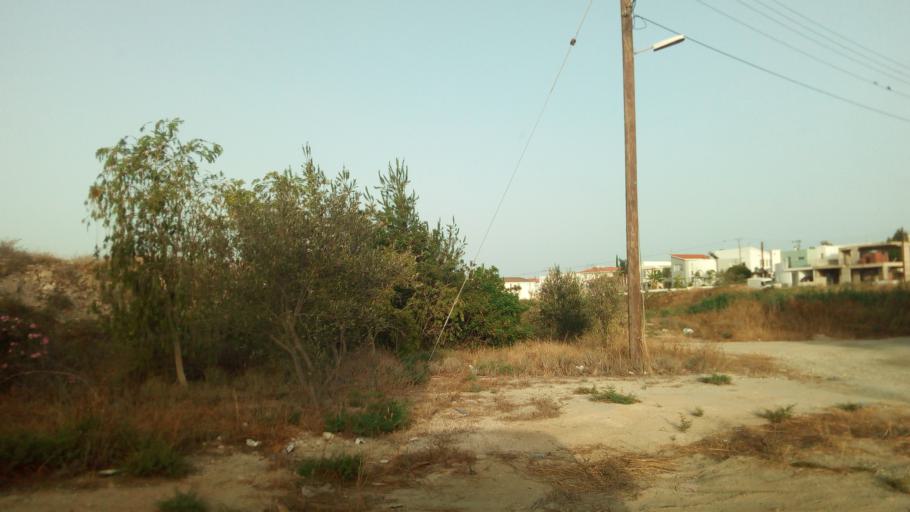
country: CY
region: Larnaka
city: Aradippou
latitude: 34.9437
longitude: 33.6064
